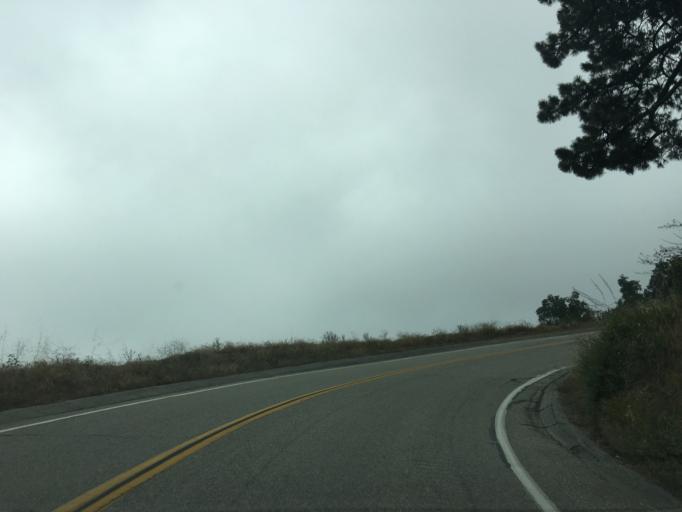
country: US
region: California
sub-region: Los Angeles County
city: Glendora
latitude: 34.1671
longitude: -117.8473
